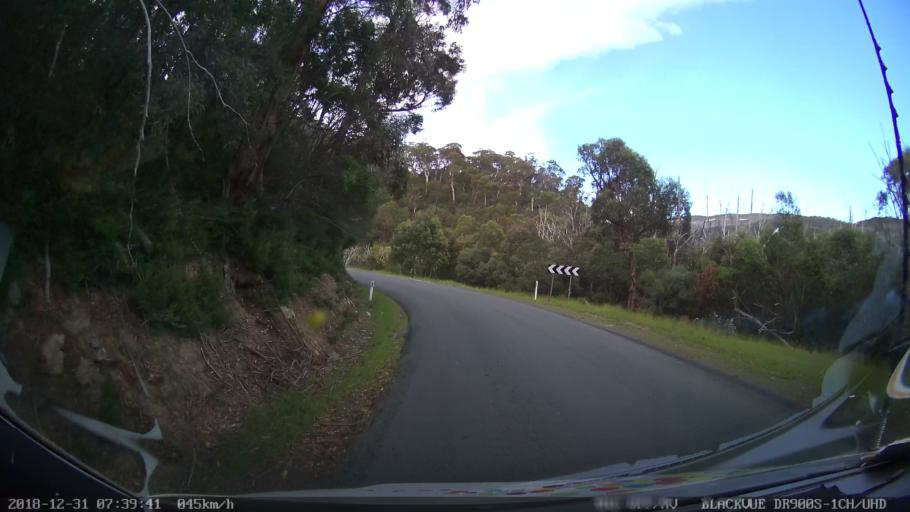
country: AU
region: New South Wales
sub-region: Snowy River
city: Jindabyne
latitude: -36.3496
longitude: 148.4193
